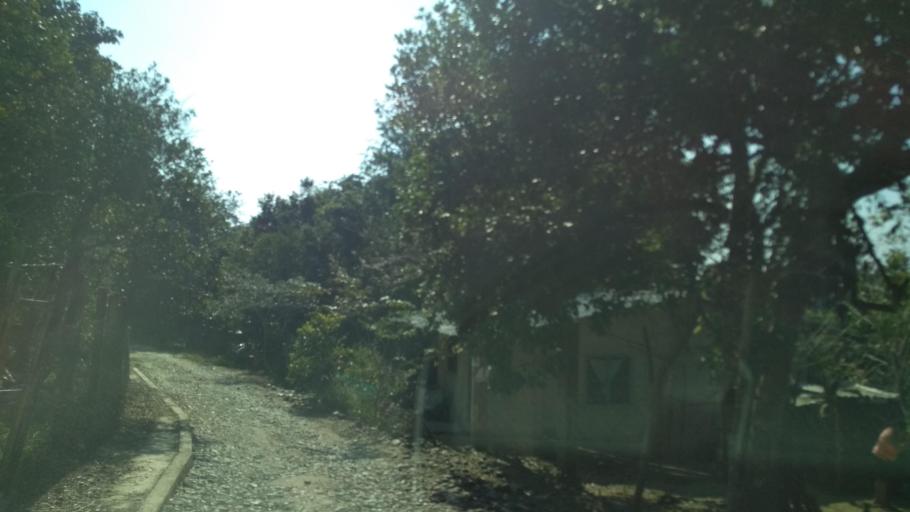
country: MX
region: Veracruz
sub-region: Papantla
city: Polutla
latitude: 20.4634
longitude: -97.1941
